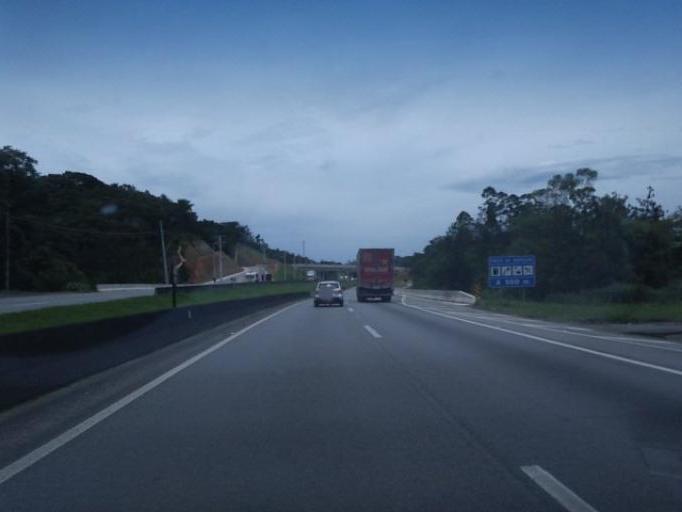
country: BR
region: Sao Paulo
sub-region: Juquitiba
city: Juquitiba
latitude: -23.9349
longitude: -47.0220
